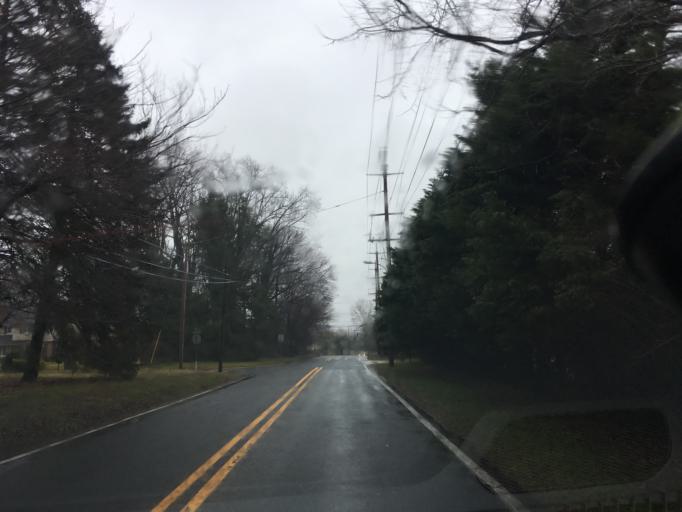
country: US
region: Delaware
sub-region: New Castle County
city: Bellefonte
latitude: 39.7852
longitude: -75.5198
